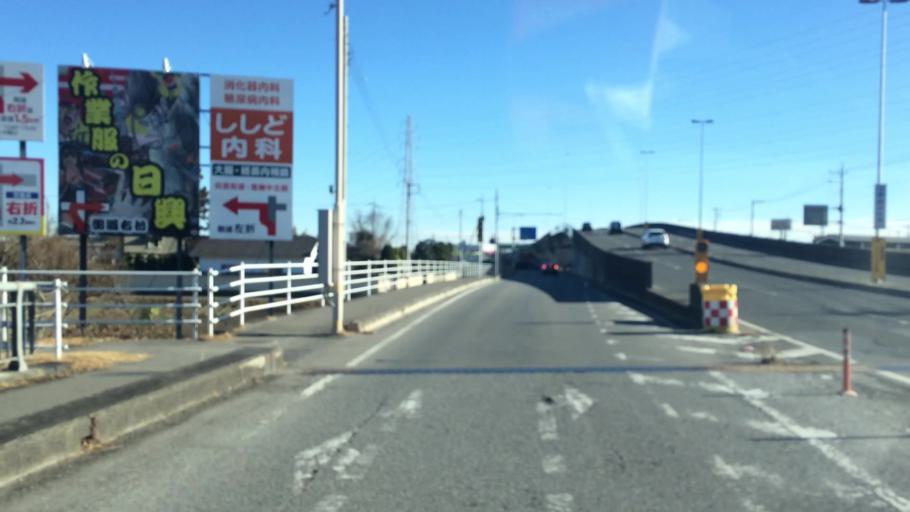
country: JP
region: Tochigi
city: Utsunomiya-shi
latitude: 36.5949
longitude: 139.8941
